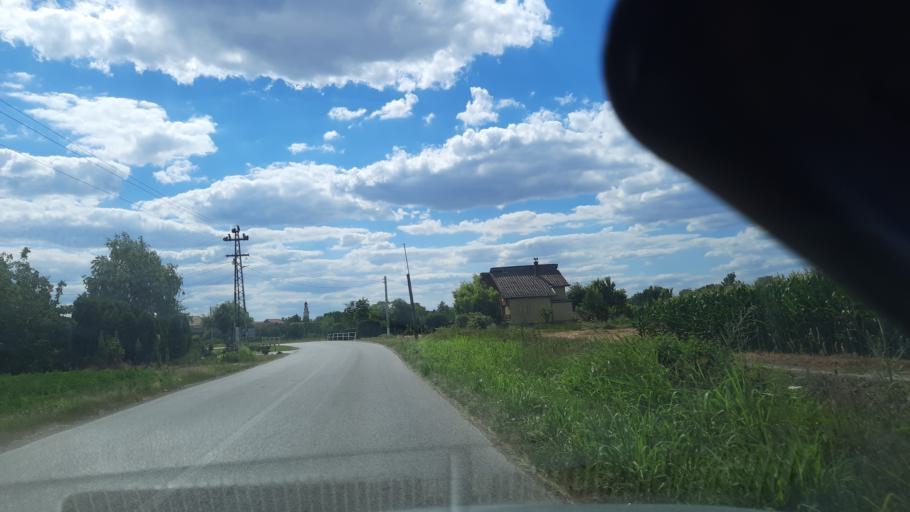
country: RS
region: Autonomna Pokrajina Vojvodina
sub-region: Sremski Okrug
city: Pecinci
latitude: 44.9065
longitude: 19.9385
